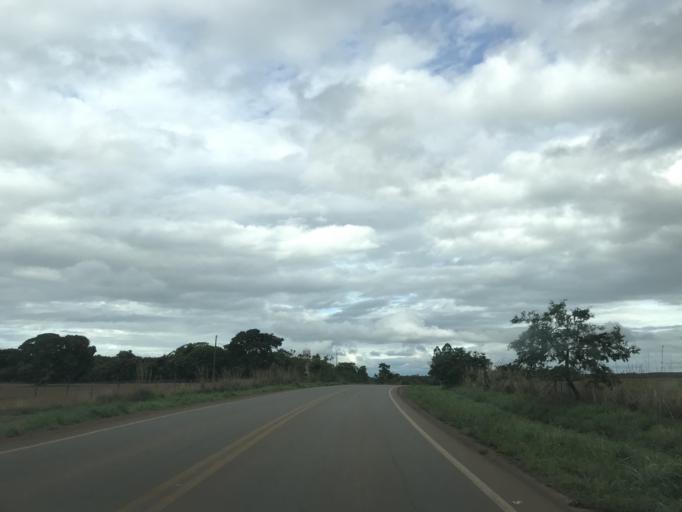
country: BR
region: Goias
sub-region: Vianopolis
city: Vianopolis
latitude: -16.7265
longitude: -48.4385
